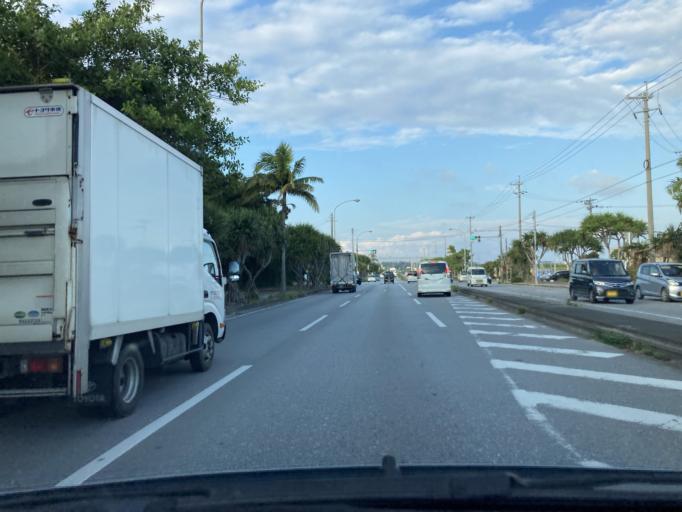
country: JP
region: Okinawa
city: Okinawa
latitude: 26.3236
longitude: 127.8334
